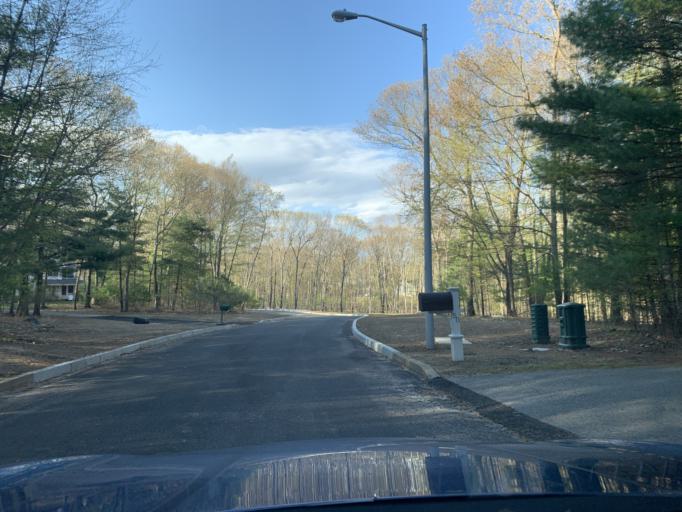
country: US
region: Rhode Island
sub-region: Washington County
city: Exeter
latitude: 41.6105
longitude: -71.5327
